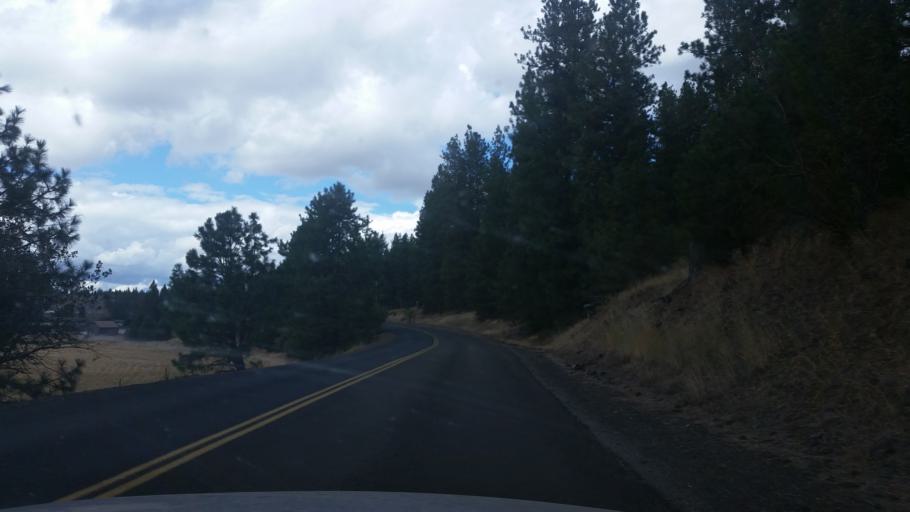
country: US
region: Washington
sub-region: Spokane County
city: Cheney
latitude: 47.5592
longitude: -117.4882
